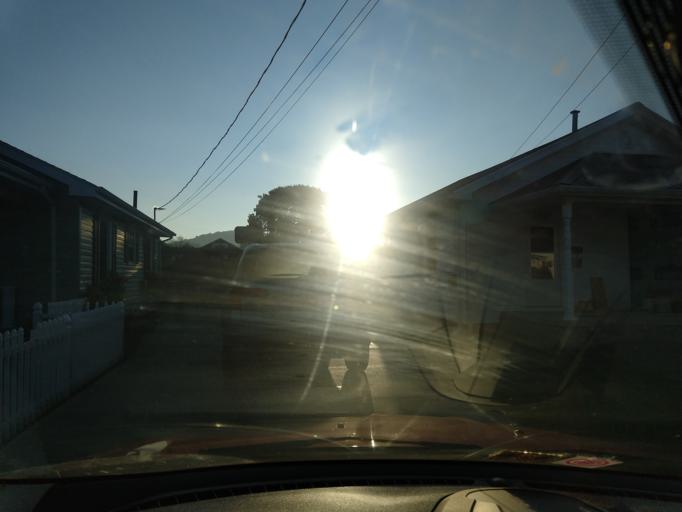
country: US
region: Virginia
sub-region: City of Covington
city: Fairlawn
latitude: 37.7636
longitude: -79.9991
